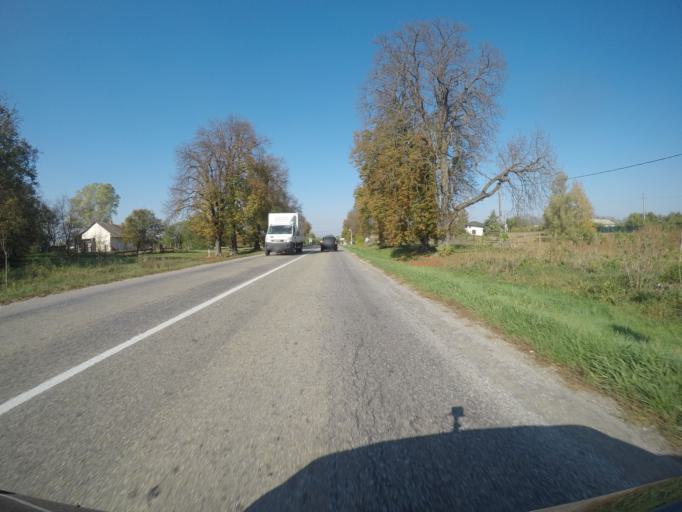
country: HU
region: Tolna
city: Szedres
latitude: 46.4687
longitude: 18.6866
